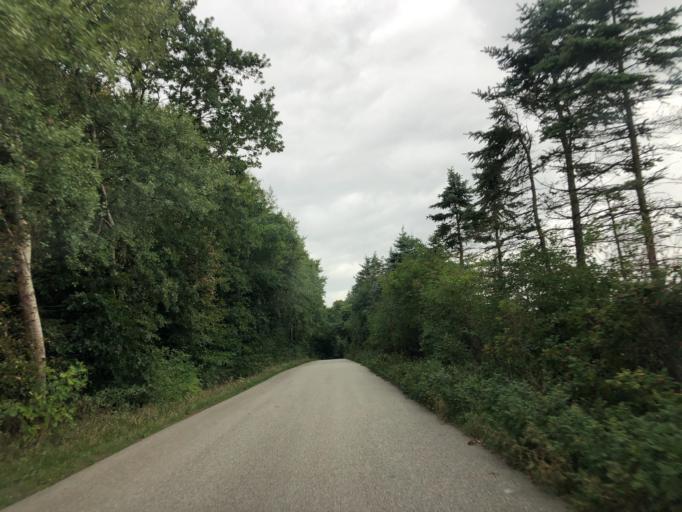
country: DK
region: Central Jutland
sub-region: Herning Kommune
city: Lind
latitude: 56.0784
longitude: 8.9776
